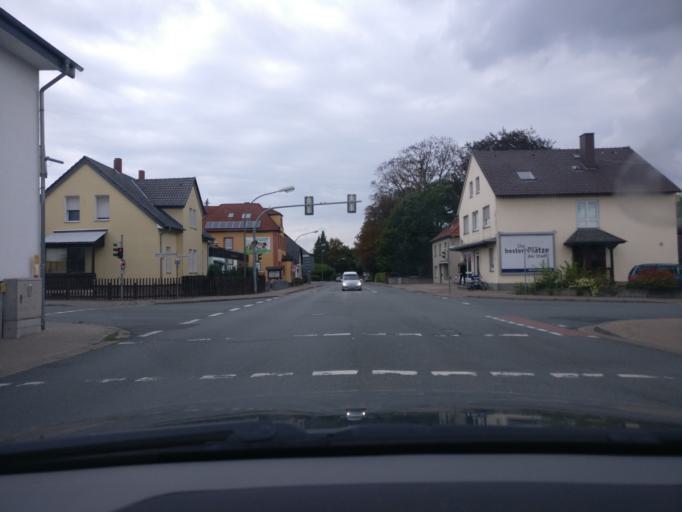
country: DE
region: Lower Saxony
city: Melle
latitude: 52.1973
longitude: 8.3349
